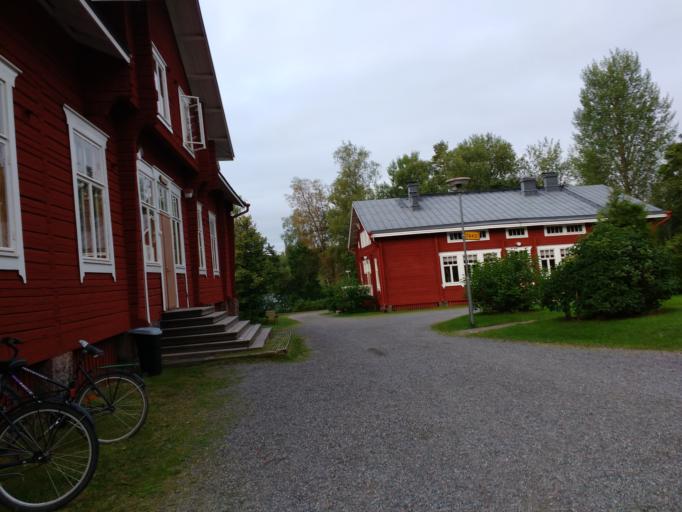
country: FI
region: Pirkanmaa
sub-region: Ylae-Pirkanmaa
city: Juupajoki
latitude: 61.8455
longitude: 24.2865
